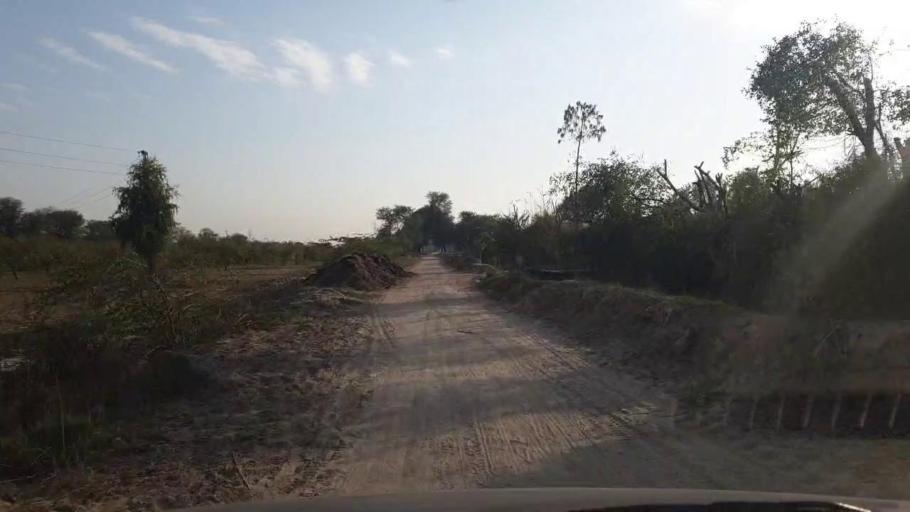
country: PK
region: Sindh
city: Sakrand
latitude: 26.0146
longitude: 68.3531
